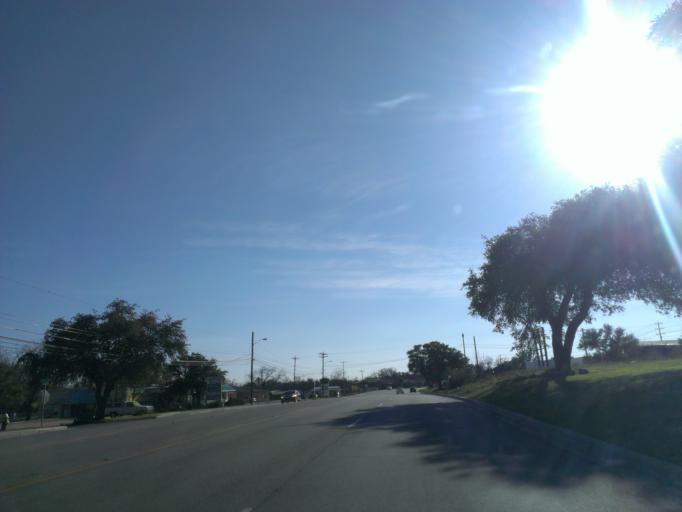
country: US
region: Texas
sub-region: Burnet County
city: Burnet
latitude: 30.7507
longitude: -98.2283
